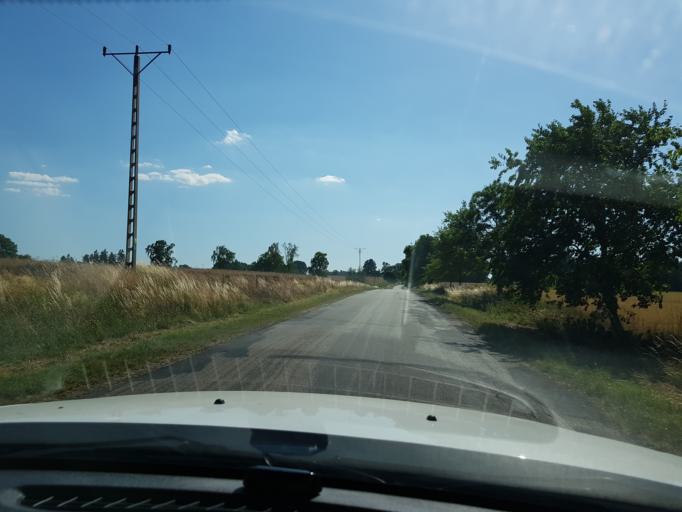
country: PL
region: West Pomeranian Voivodeship
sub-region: Powiat bialogardzki
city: Karlino
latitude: 53.9449
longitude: 15.8516
